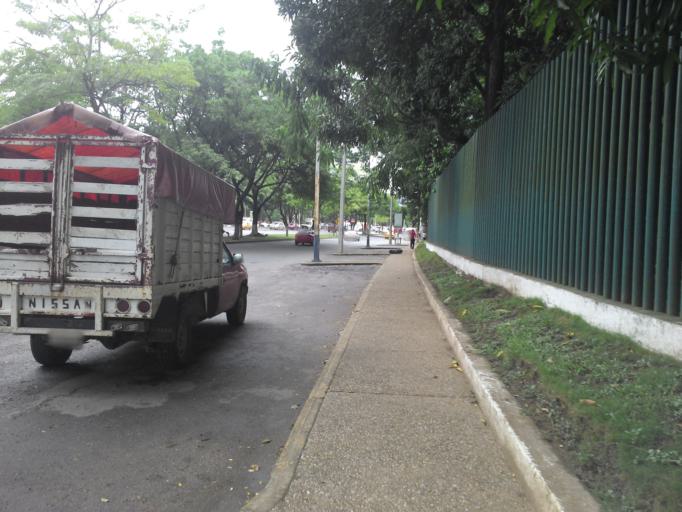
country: MX
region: Tabasco
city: Villahermosa
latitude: 18.0006
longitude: -92.9366
